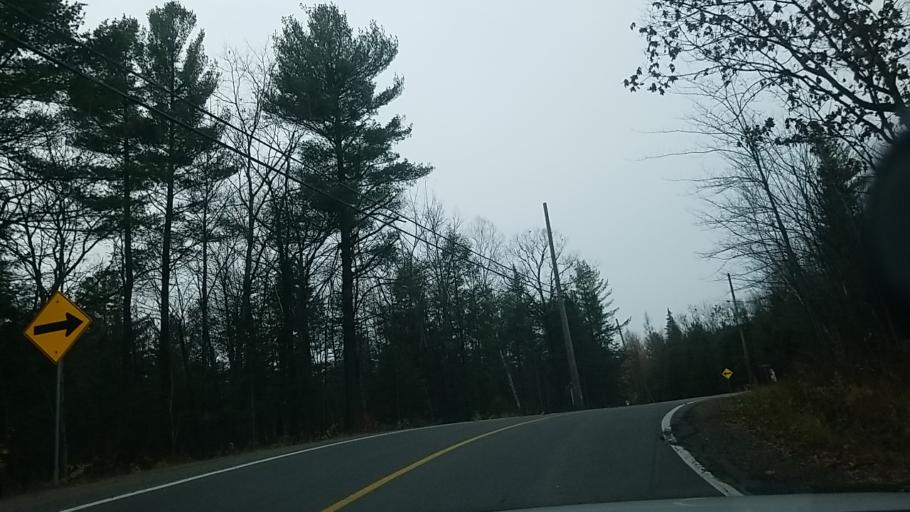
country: CA
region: Quebec
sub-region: Laurentides
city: Saint-Colomban
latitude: 45.7877
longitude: -74.1219
